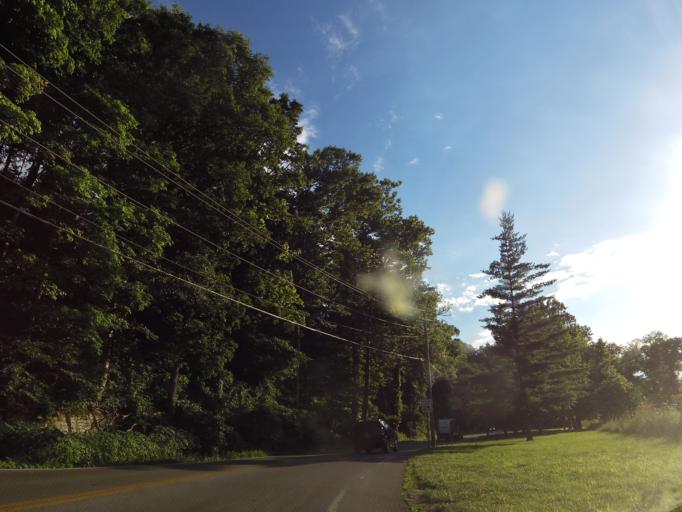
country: US
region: Missouri
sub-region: Saint Charles County
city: Weldon Spring
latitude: 38.6493
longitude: -90.6713
